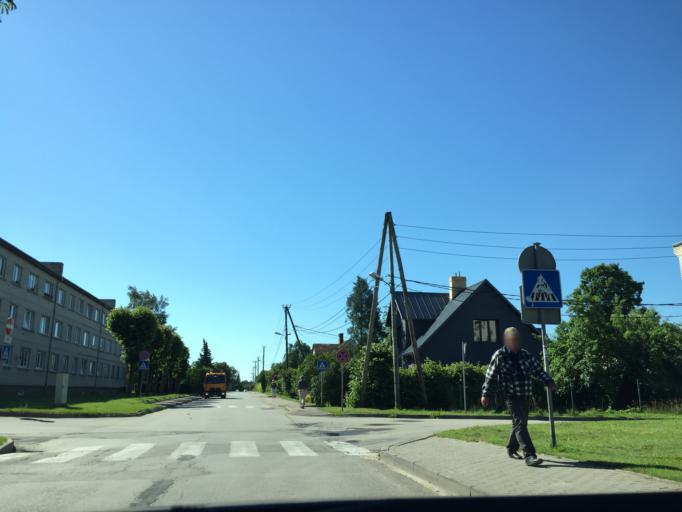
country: LV
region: Bauskas Rajons
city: Bauska
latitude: 56.4058
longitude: 24.1899
